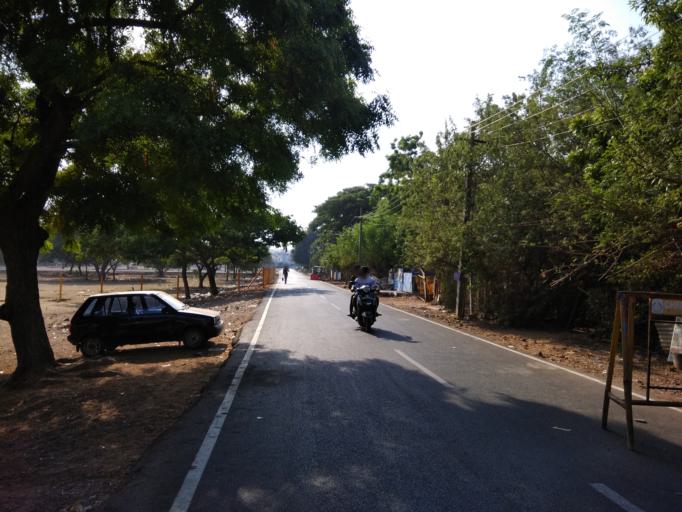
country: IN
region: Tamil Nadu
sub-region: Kancheepuram
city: Saint Thomas Mount
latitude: 13.0150
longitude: 80.1878
